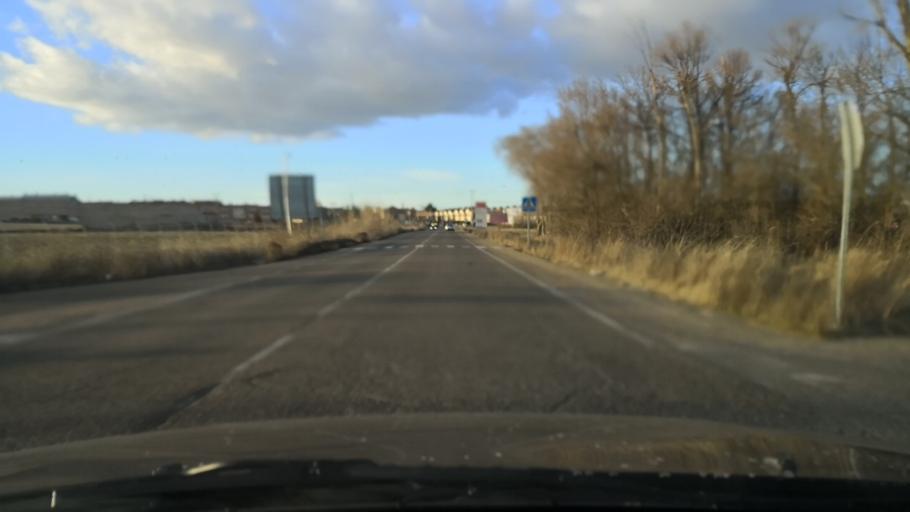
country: ES
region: Castille and Leon
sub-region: Provincia de Valladolid
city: Medina del Campo
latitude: 41.2969
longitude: -4.9044
